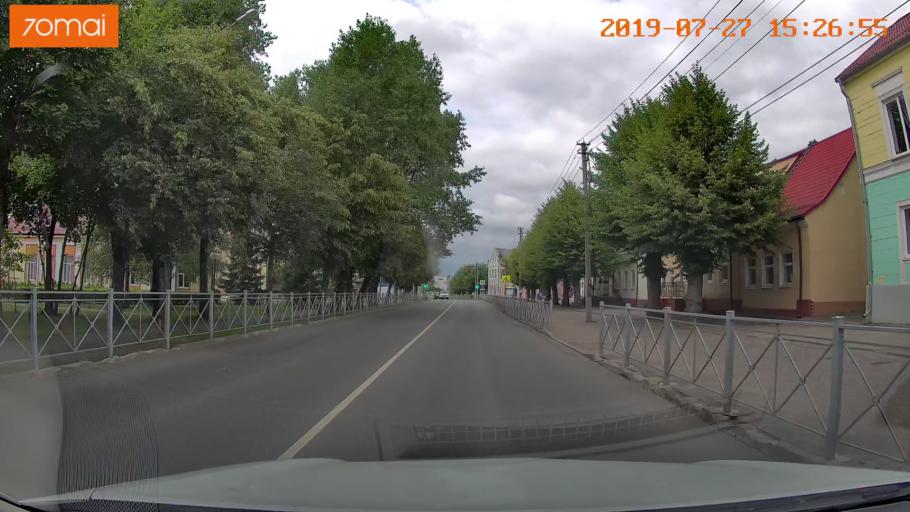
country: RU
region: Kaliningrad
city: Nesterov
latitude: 54.6333
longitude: 22.5689
